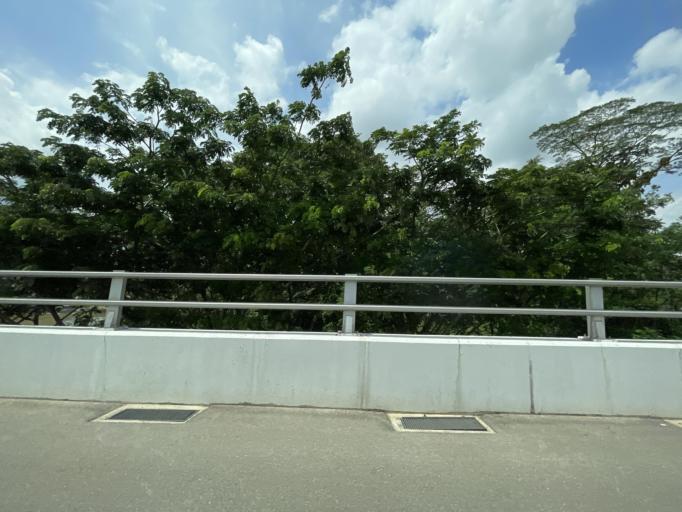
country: MY
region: Johor
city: Johor Bahru
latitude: 1.3627
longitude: 103.7674
